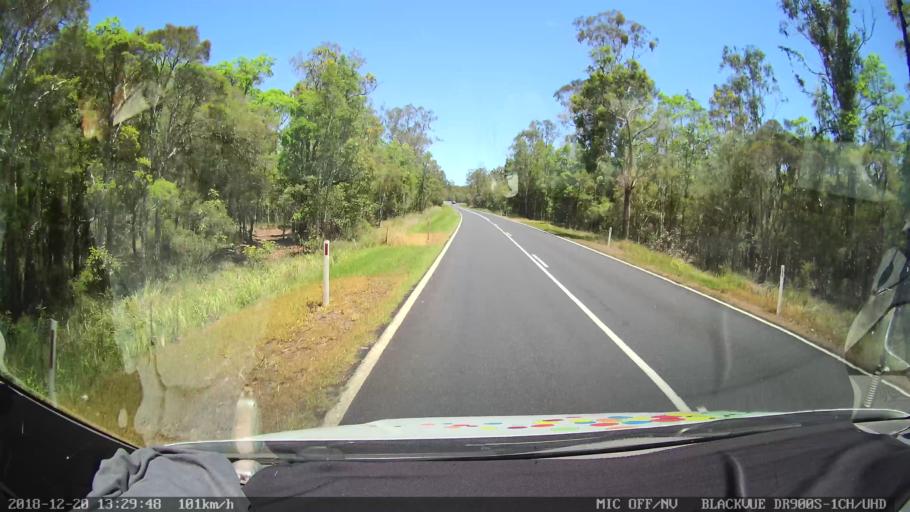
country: AU
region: New South Wales
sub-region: Clarence Valley
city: Gordon
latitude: -29.1945
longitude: 152.9910
